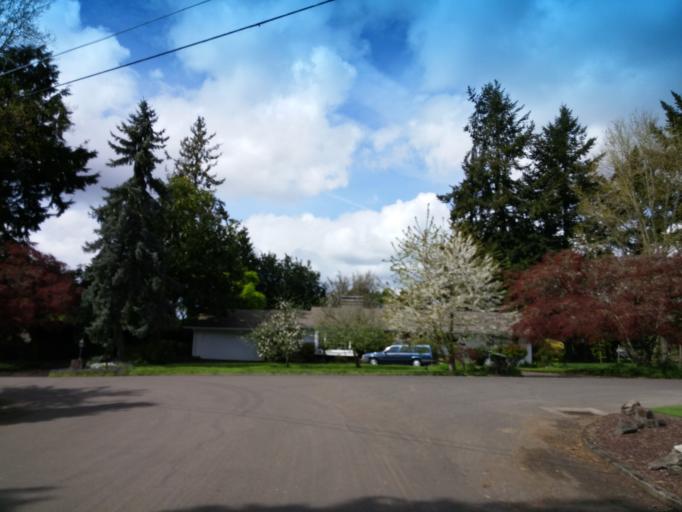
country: US
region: Oregon
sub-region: Washington County
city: Cedar Hills
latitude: 45.5142
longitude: -122.7990
